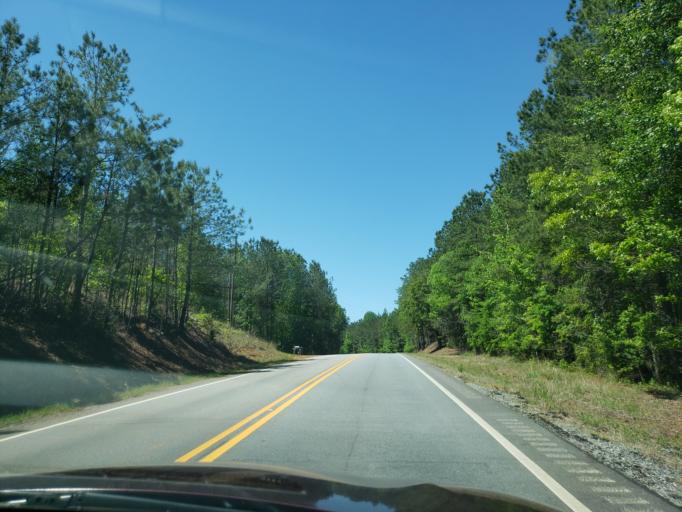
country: US
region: Alabama
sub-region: Elmore County
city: Tallassee
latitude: 32.6654
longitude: -85.7964
